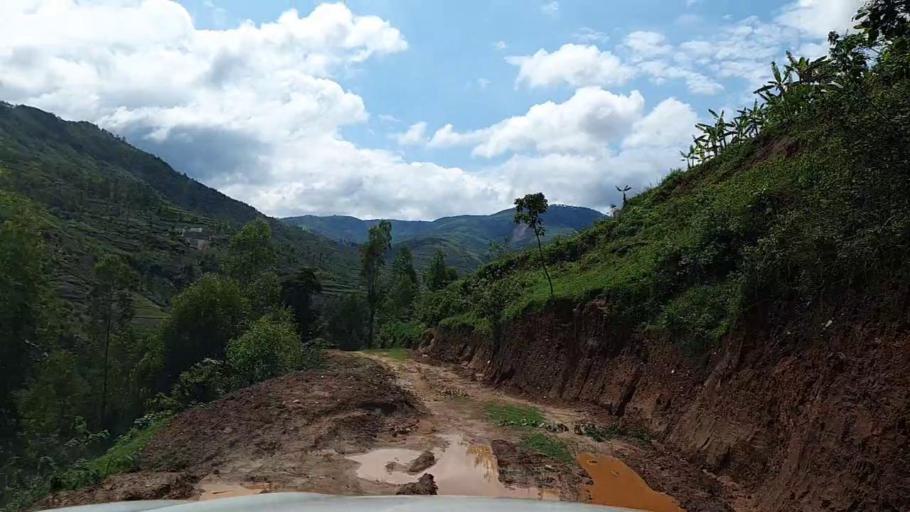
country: RW
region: Southern Province
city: Gikongoro
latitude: -2.3616
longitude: 29.5416
